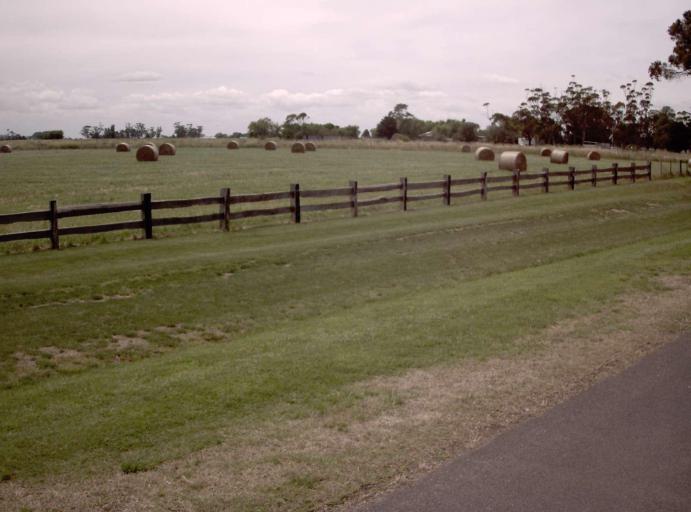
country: AU
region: Victoria
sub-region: Wellington
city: Sale
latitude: -38.0675
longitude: 147.0329
